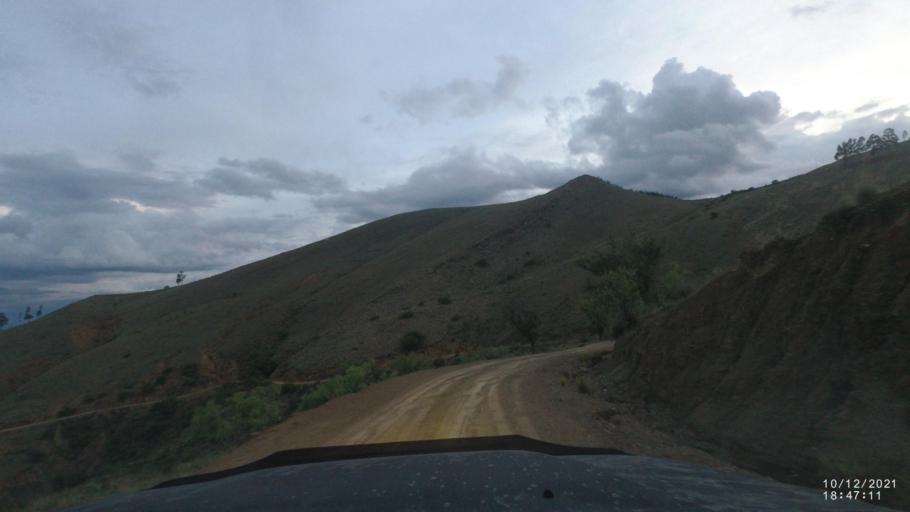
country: BO
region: Cochabamba
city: Tarata
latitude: -17.8793
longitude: -65.9741
